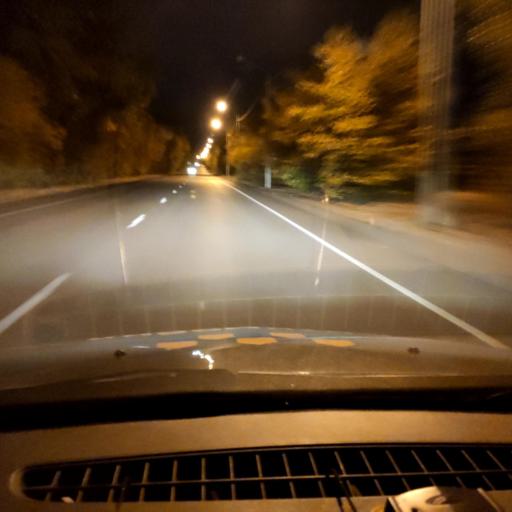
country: RU
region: Voronezj
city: Voronezh
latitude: 51.6065
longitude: 39.1789
